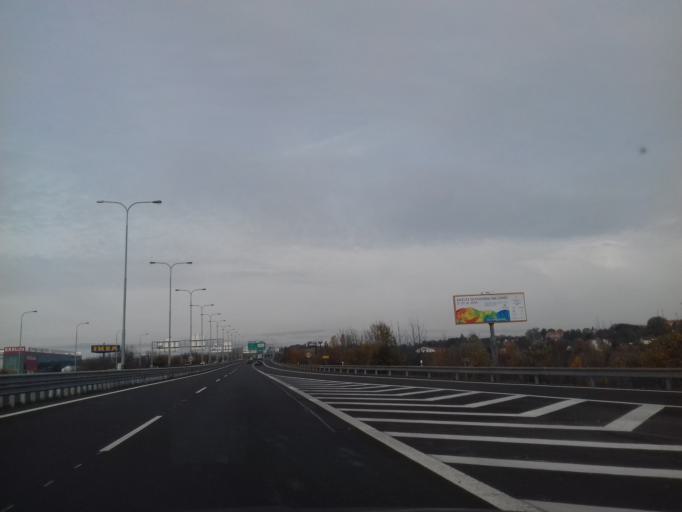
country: CZ
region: Praha
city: Cerny Most
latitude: 50.1021
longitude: 14.5911
